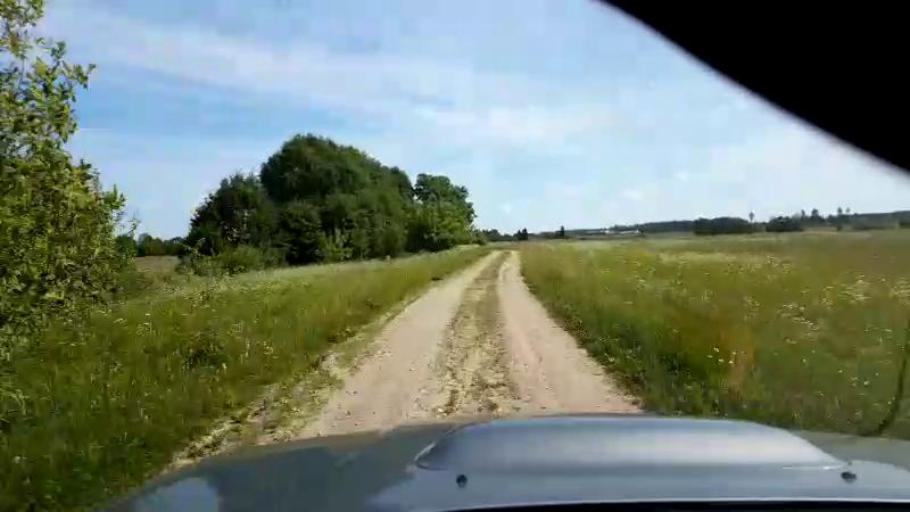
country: EE
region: Paernumaa
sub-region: Sauga vald
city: Sauga
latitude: 58.4981
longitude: 24.5422
